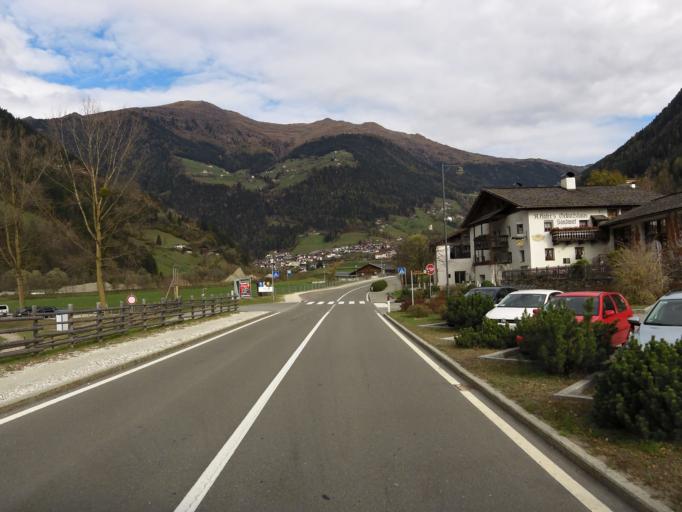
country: IT
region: Trentino-Alto Adige
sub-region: Bolzano
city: San Leonardo in Passiria
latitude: 46.8011
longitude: 11.2381
